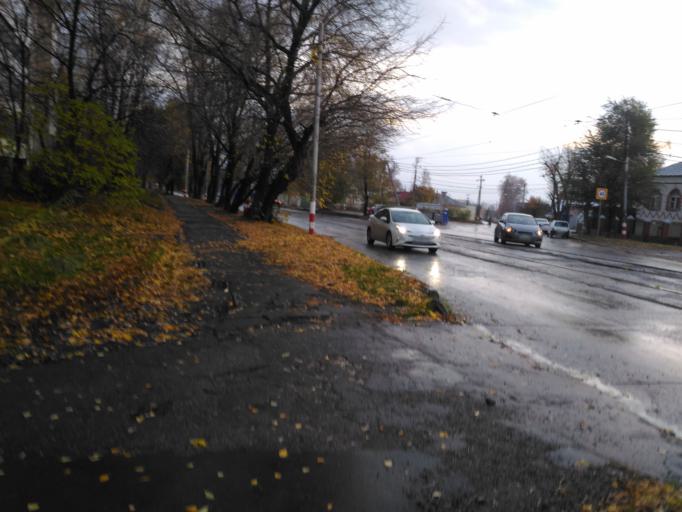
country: RU
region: Ulyanovsk
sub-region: Ulyanovskiy Rayon
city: Ulyanovsk
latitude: 54.3311
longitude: 48.3852
